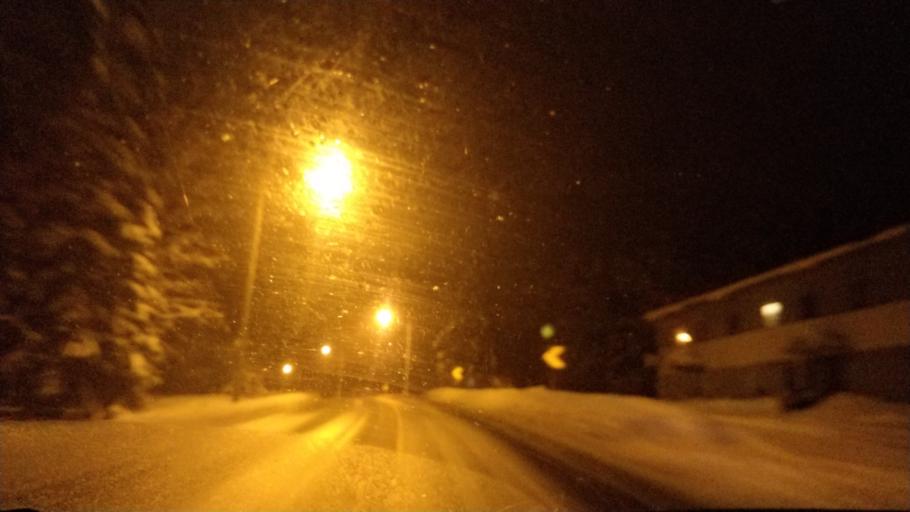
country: FI
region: Lapland
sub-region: Rovaniemi
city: Rovaniemi
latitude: 66.2749
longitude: 25.3300
